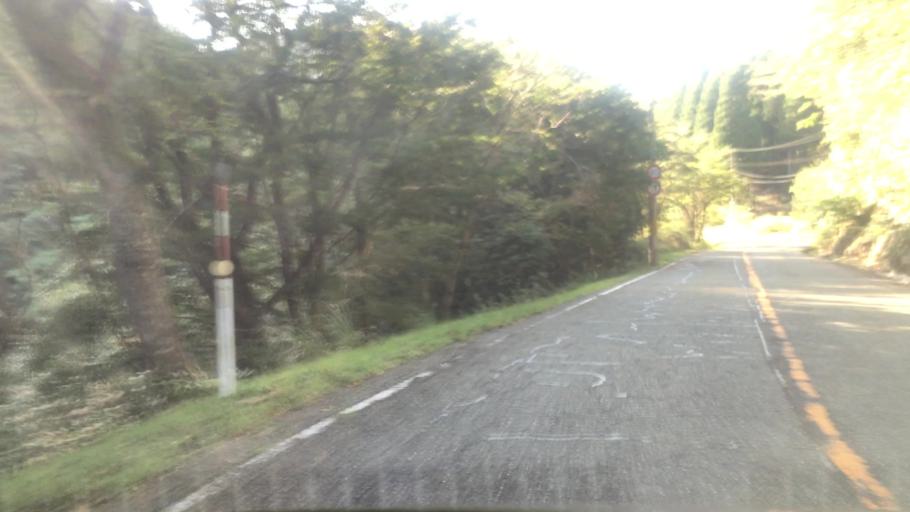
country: JP
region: Hyogo
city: Toyooka
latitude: 35.6200
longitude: 134.8703
